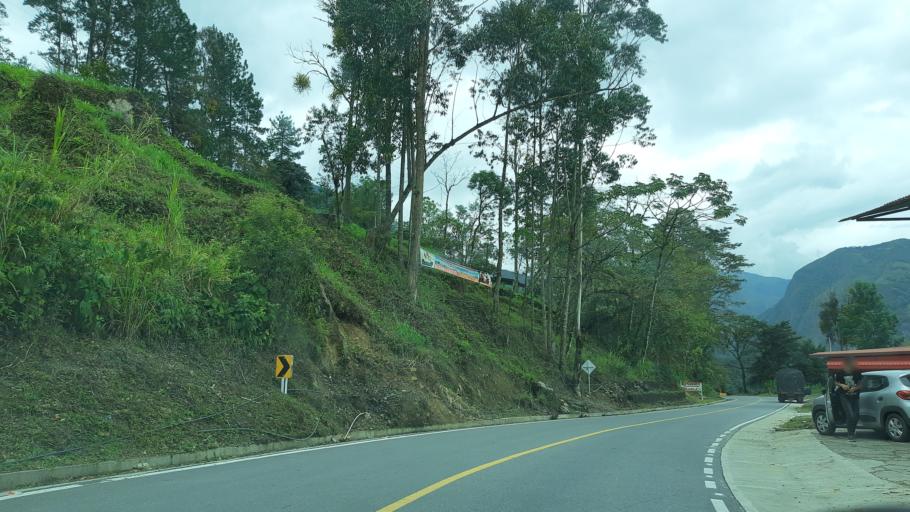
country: CO
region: Boyaca
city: Chivor
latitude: 4.9560
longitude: -73.3108
